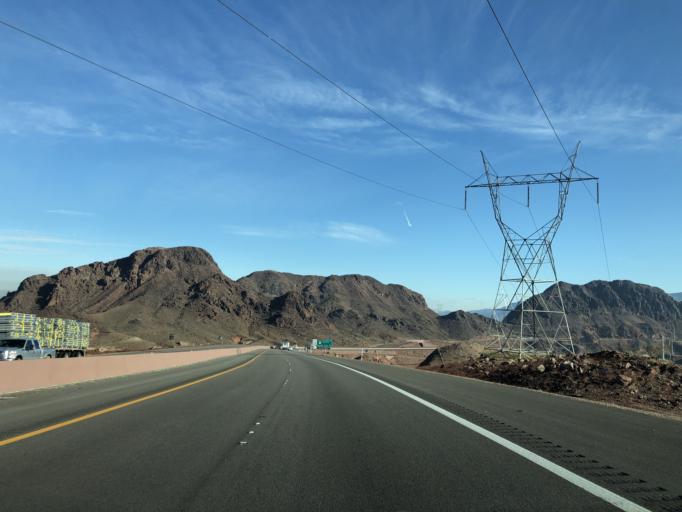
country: US
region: Nevada
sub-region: Clark County
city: Boulder City
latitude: 36.0056
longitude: -114.7816
